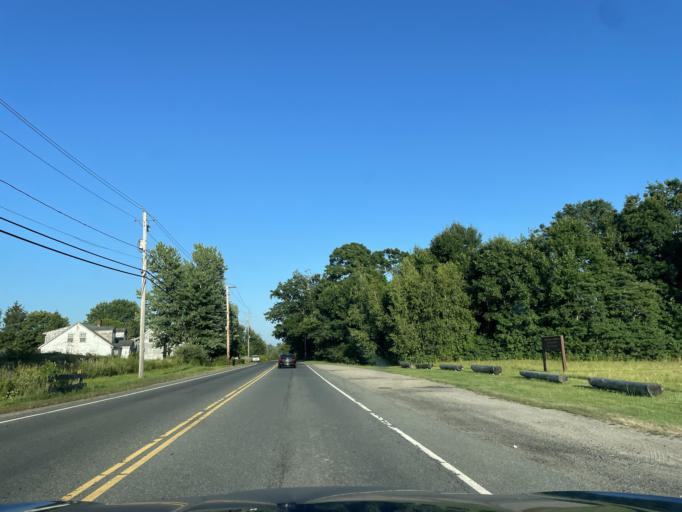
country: US
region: Massachusetts
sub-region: Plymouth County
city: West Bridgewater
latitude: 42.0200
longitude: -71.0017
